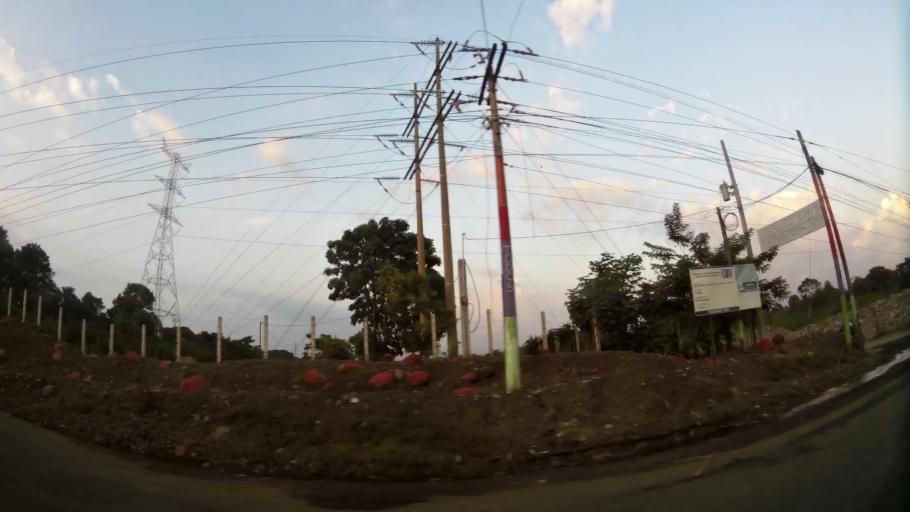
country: GT
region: Retalhuleu
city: San Sebastian
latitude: 14.5757
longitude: -91.6341
